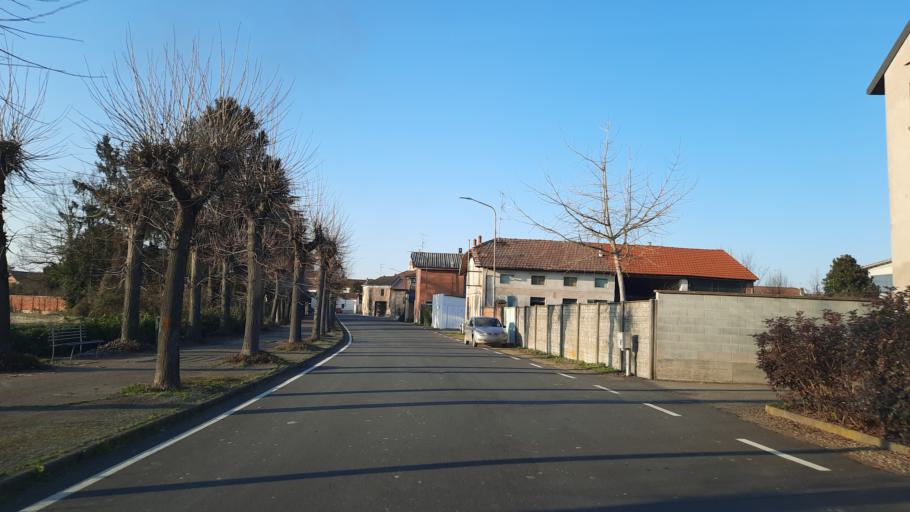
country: IT
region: Piedmont
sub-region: Provincia di Vercelli
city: Costanzana
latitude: 45.2337
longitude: 8.3706
